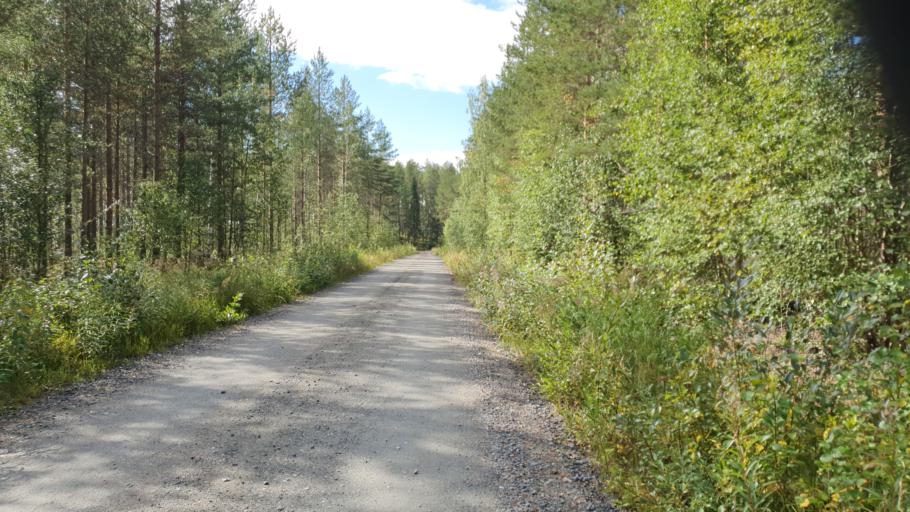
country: FI
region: Kainuu
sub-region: Kehys-Kainuu
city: Kuhmo
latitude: 64.1312
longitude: 29.3515
